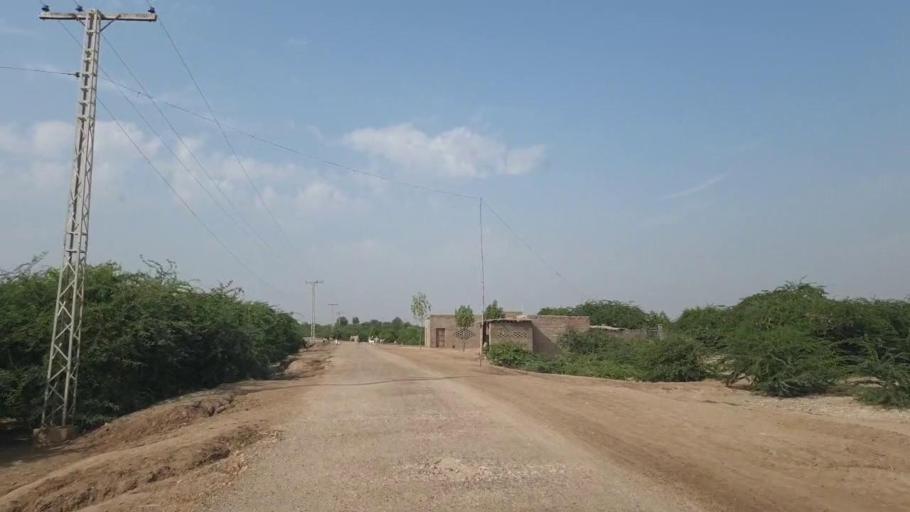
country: PK
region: Sindh
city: Digri
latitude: 25.0066
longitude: 69.0650
